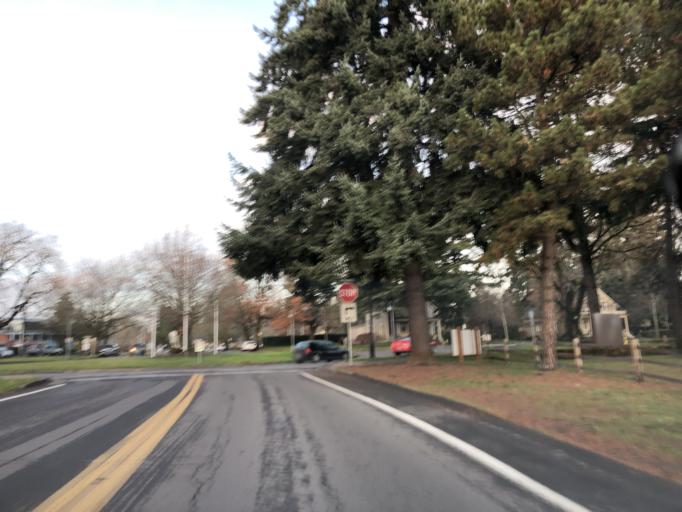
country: US
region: Washington
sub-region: Clark County
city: Vancouver
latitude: 45.6282
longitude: -122.6635
